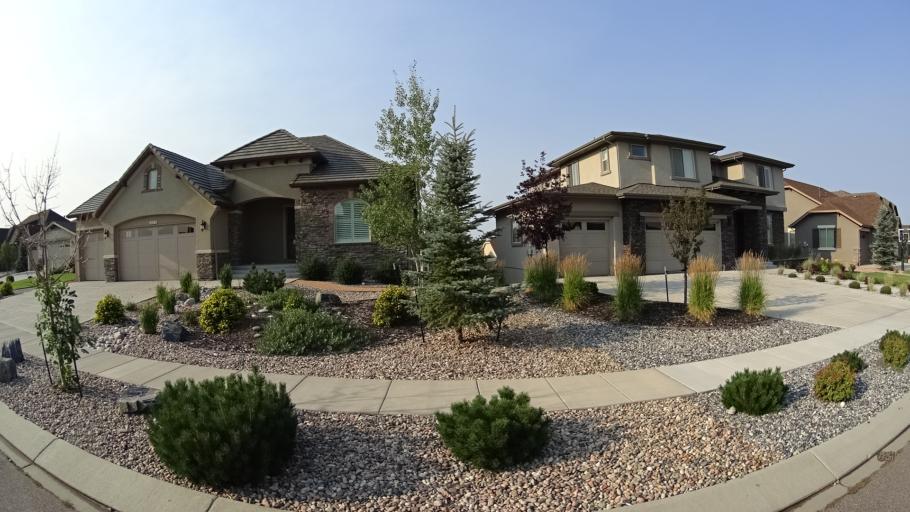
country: US
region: Colorado
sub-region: El Paso County
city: Black Forest
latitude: 38.9753
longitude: -104.7299
